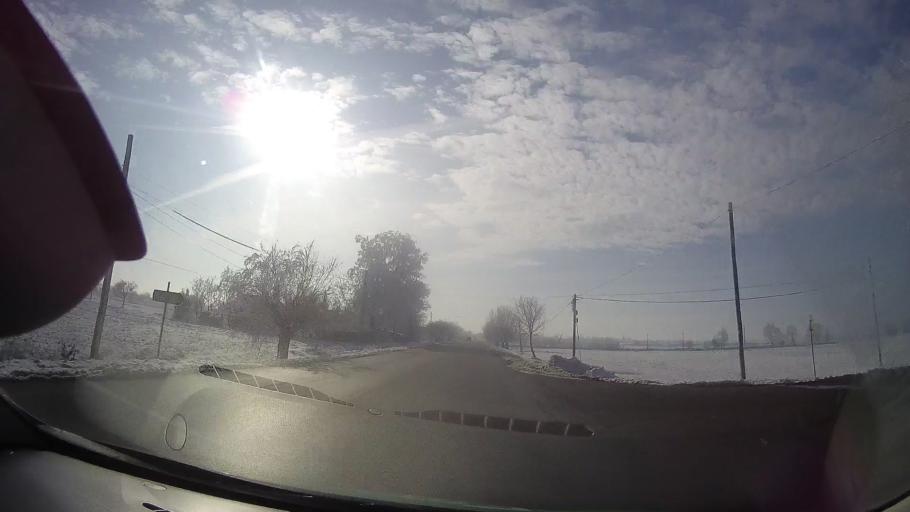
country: RO
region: Neamt
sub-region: Comuna Timisesti
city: Timisesti
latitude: 47.2412
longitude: 26.5397
